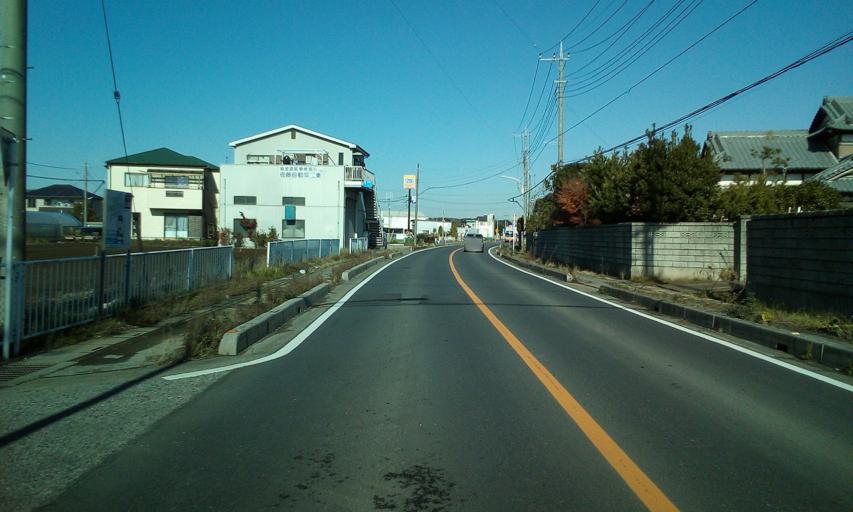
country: JP
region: Chiba
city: Nagareyama
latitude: 35.8647
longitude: 139.8883
